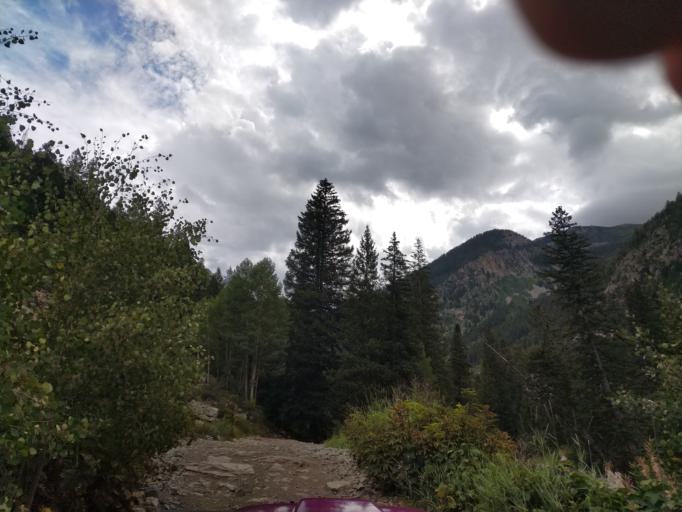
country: US
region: Colorado
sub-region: Gunnison County
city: Crested Butte
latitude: 39.0559
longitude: -107.1311
